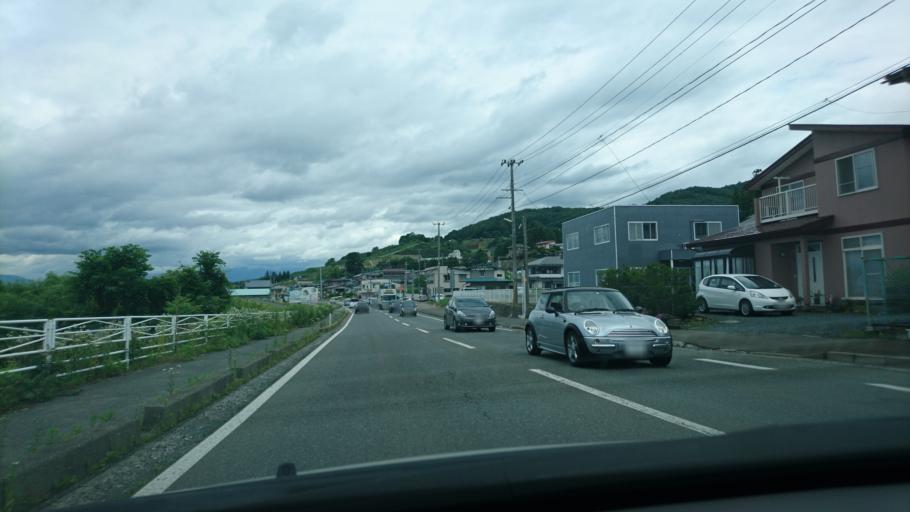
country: JP
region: Iwate
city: Morioka-shi
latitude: 39.6569
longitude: 141.1818
